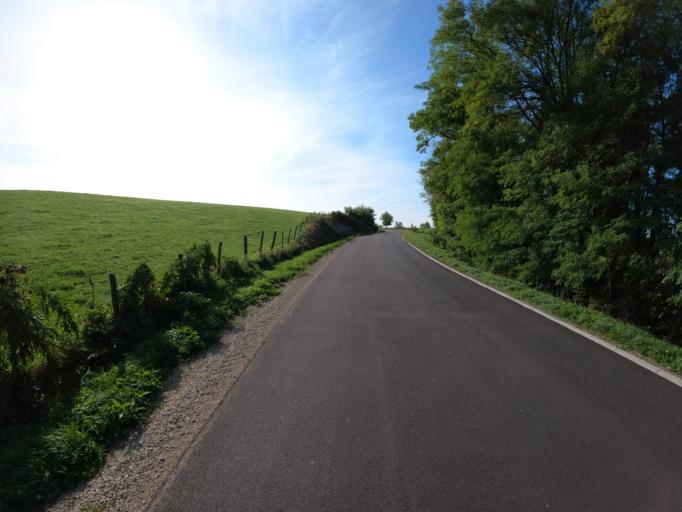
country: FR
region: Franche-Comte
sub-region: Departement du Jura
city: Bletterans
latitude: 46.7344
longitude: 5.5030
